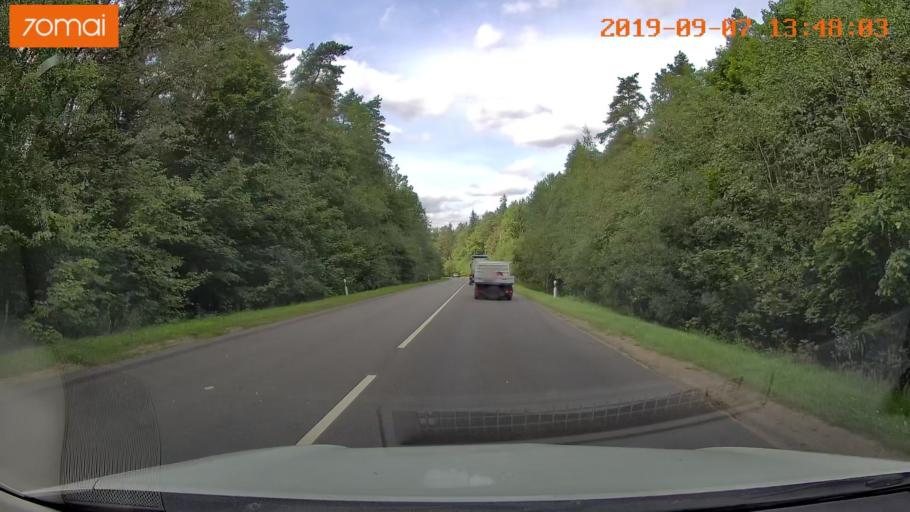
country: LT
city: Baltoji Voke
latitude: 54.6005
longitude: 25.2072
